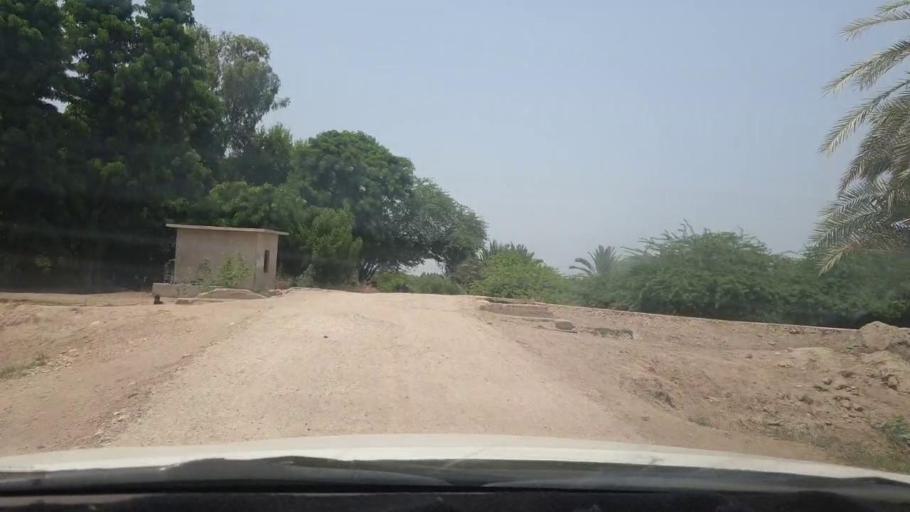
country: PK
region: Sindh
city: Khairpur
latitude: 27.5039
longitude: 68.8643
